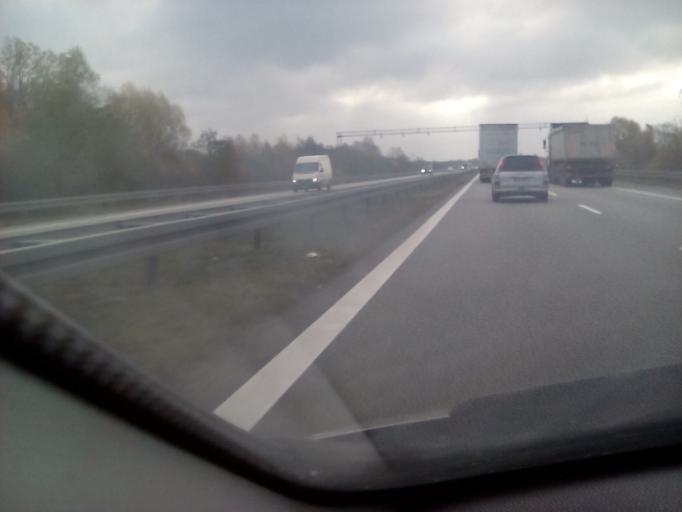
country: PL
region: Masovian Voivodeship
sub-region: Powiat bialobrzeski
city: Promna
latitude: 51.6667
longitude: 20.9544
